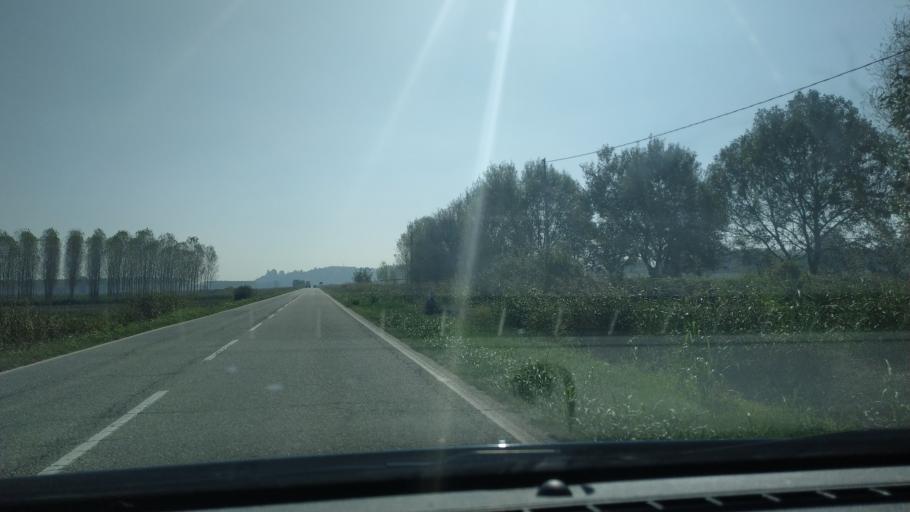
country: IT
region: Piedmont
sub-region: Provincia di Alessandria
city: Giarole
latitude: 45.0781
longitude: 8.5680
